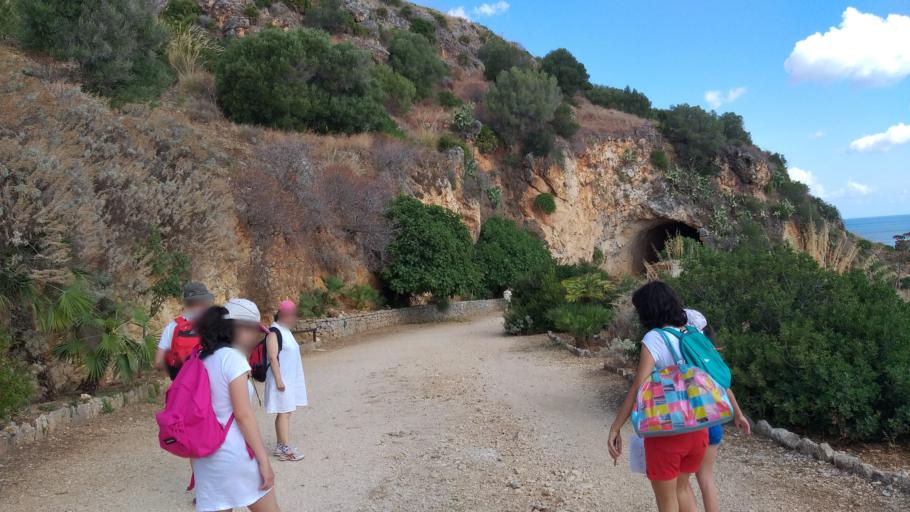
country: IT
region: Sicily
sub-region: Trapani
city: Castelluzzo
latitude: 38.0821
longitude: 12.8078
